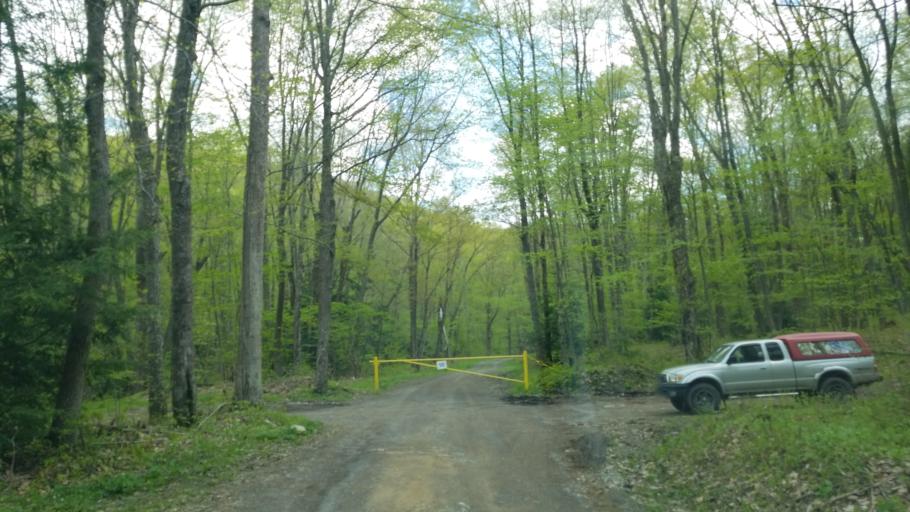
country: US
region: Pennsylvania
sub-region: Clearfield County
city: Shiloh
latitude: 41.2091
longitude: -78.1336
